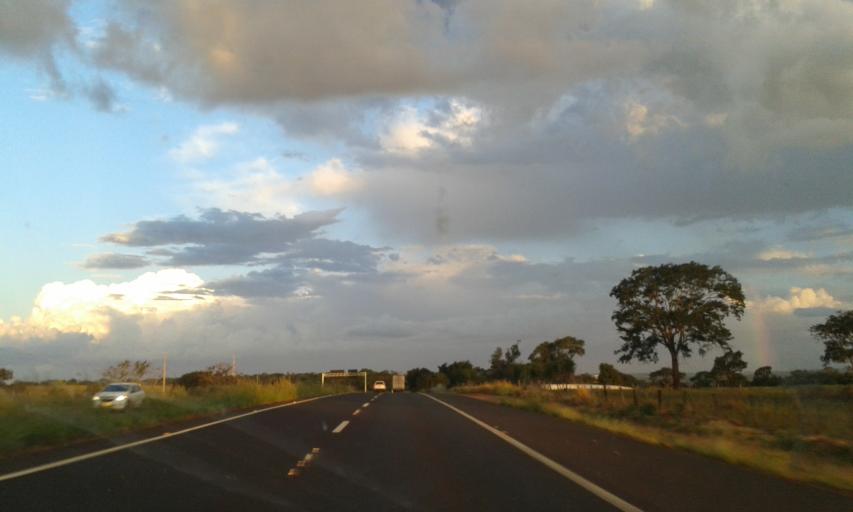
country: BR
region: Minas Gerais
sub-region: Monte Alegre De Minas
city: Monte Alegre de Minas
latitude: -18.8798
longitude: -48.7427
